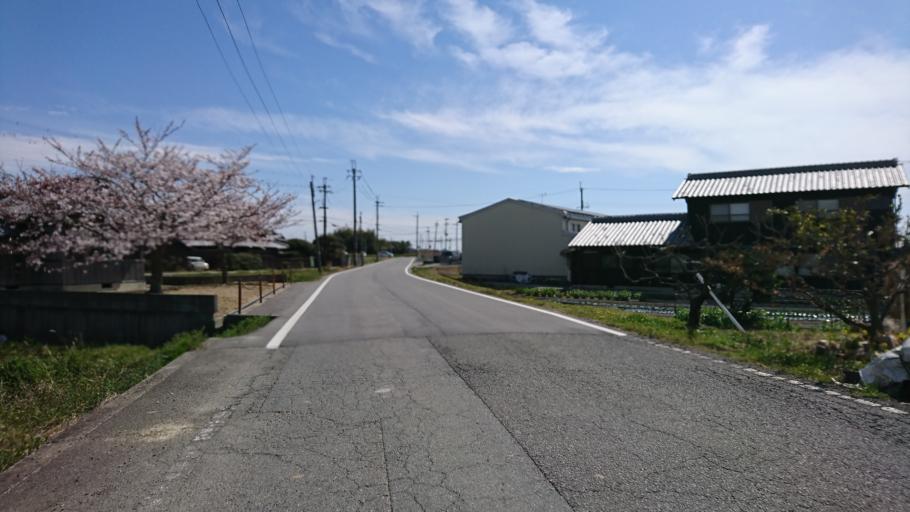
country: JP
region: Hyogo
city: Miki
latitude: 34.7546
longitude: 134.9350
